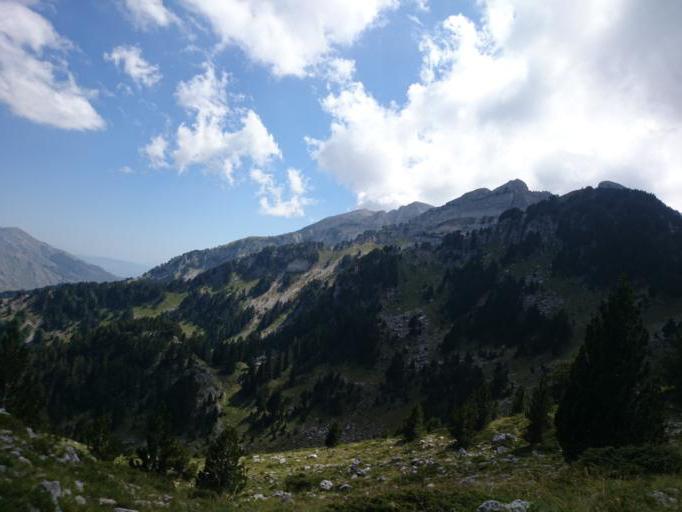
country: AL
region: Berat
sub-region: Rrethi i Beratit
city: Polican
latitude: 40.6628
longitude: 20.1599
